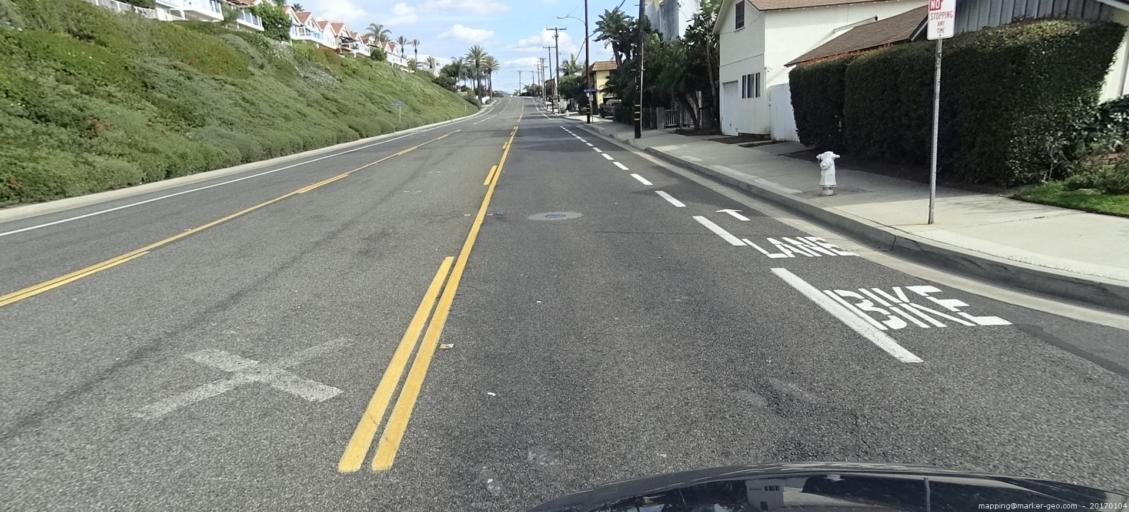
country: US
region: California
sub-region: Orange County
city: Dana Point
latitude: 33.4727
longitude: -117.6972
